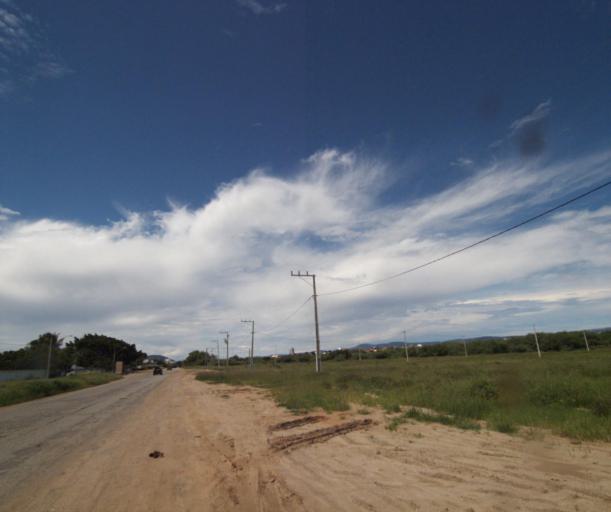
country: BR
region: Bahia
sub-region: Guanambi
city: Guanambi
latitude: -14.2457
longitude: -42.7818
